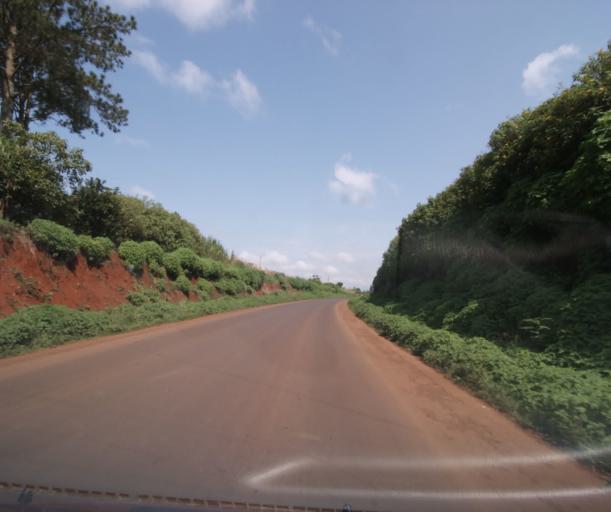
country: CM
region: West
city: Bansoa
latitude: 5.4957
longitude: 10.2558
